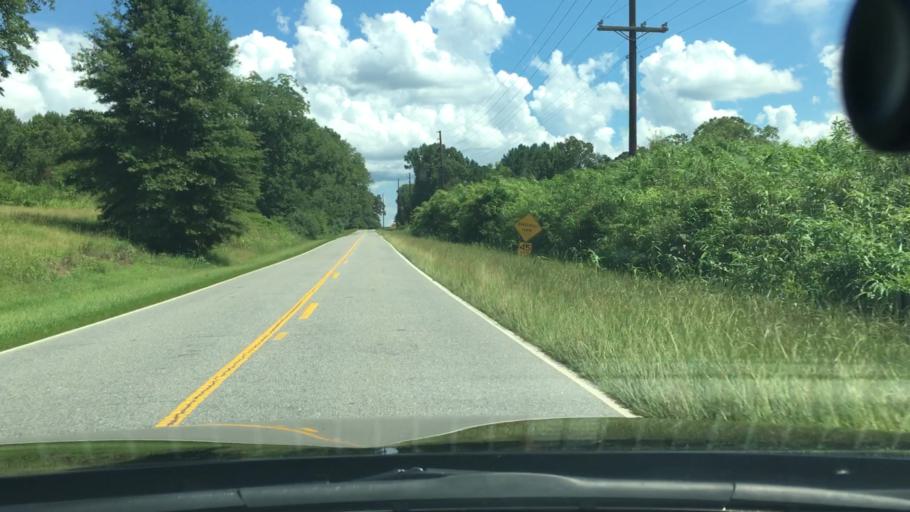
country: US
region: Georgia
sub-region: Putnam County
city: Jefferson
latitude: 33.3805
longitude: -83.2527
